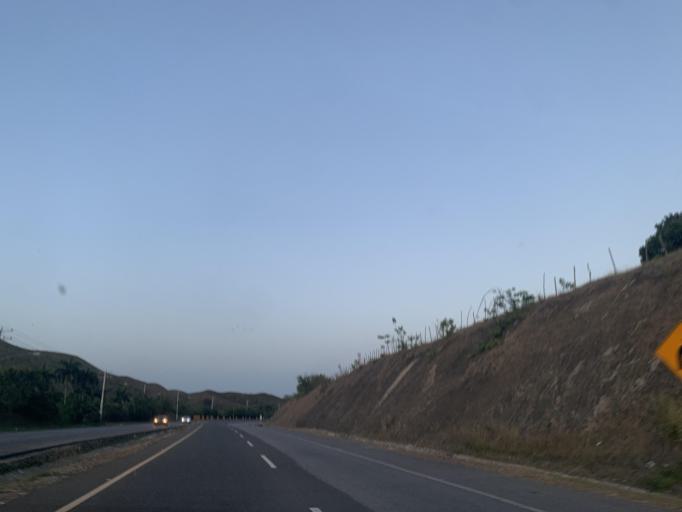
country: DO
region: Puerto Plata
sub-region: Puerto Plata
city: Puerto Plata
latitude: 19.8275
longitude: -70.7536
